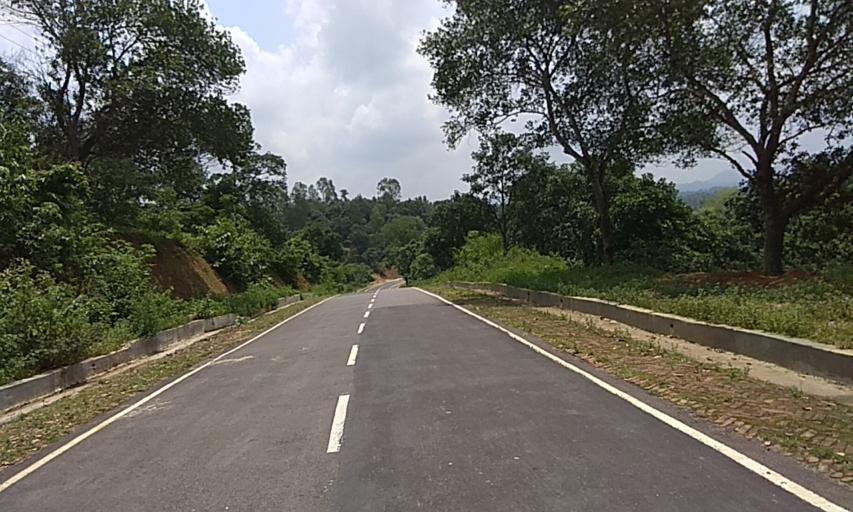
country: BD
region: Chittagong
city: Manikchari
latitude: 22.9386
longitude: 91.9016
